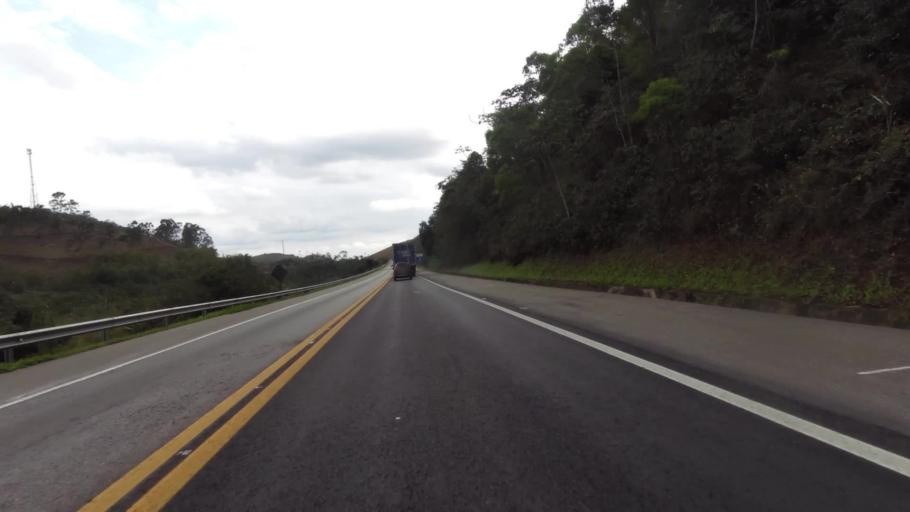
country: BR
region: Rio de Janeiro
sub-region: Rio Das Ostras
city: Rio das Ostras
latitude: -22.4604
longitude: -42.0632
